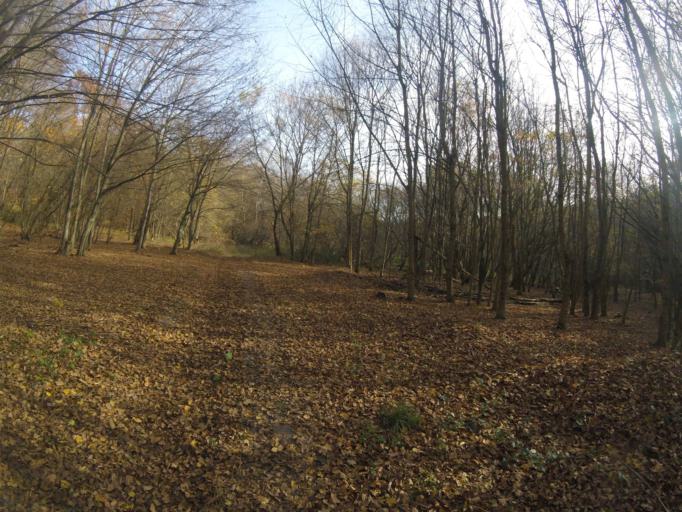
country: HU
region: Borsod-Abauj-Zemplen
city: Sarospatak
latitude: 48.4313
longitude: 21.5131
